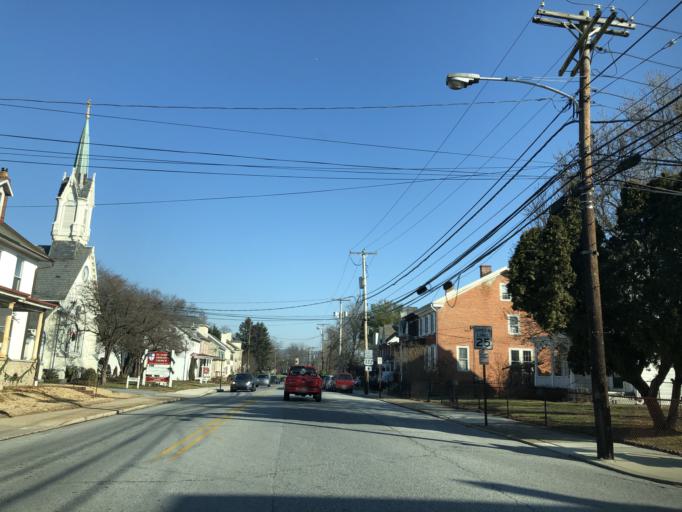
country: US
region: Pennsylvania
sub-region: Chester County
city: Downingtown
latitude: 40.0094
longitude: -75.6976
